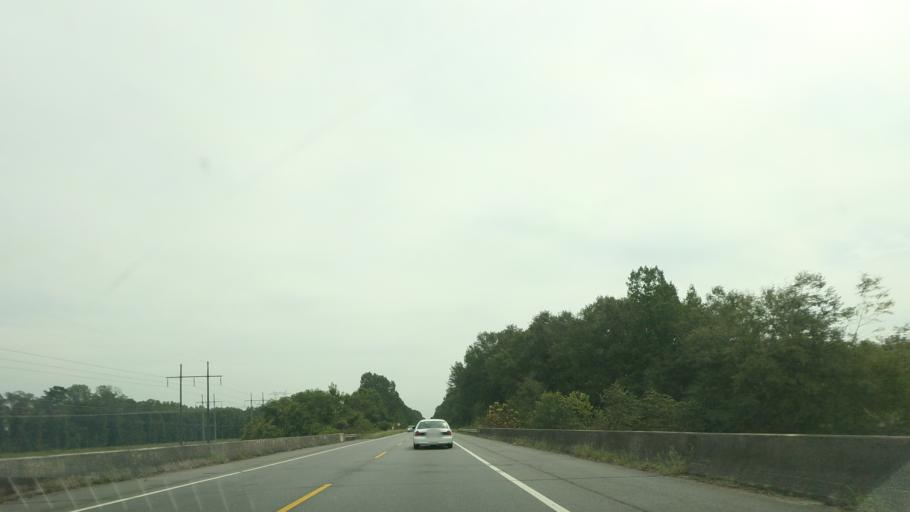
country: US
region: Georgia
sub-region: Houston County
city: Robins Air Force Base
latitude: 32.5424
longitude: -83.5298
